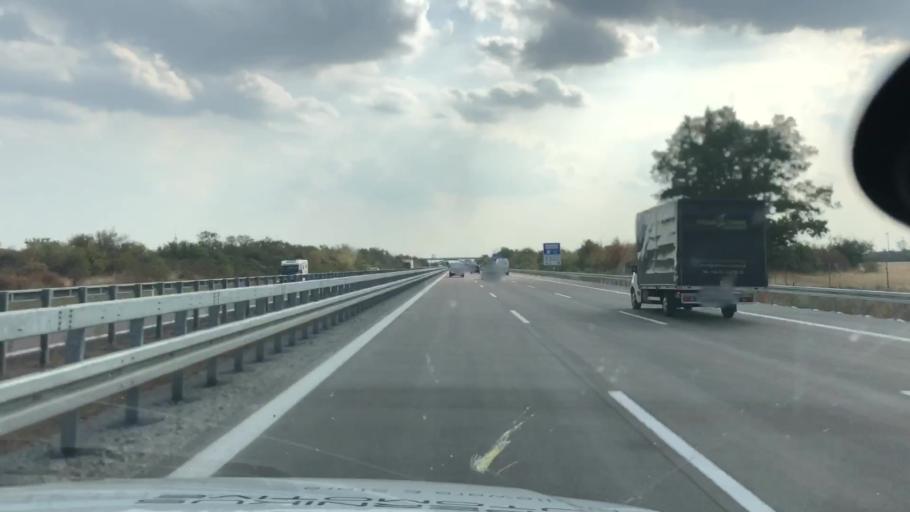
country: DE
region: Saxony-Anhalt
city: Thalheim
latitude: 51.6627
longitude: 12.2036
